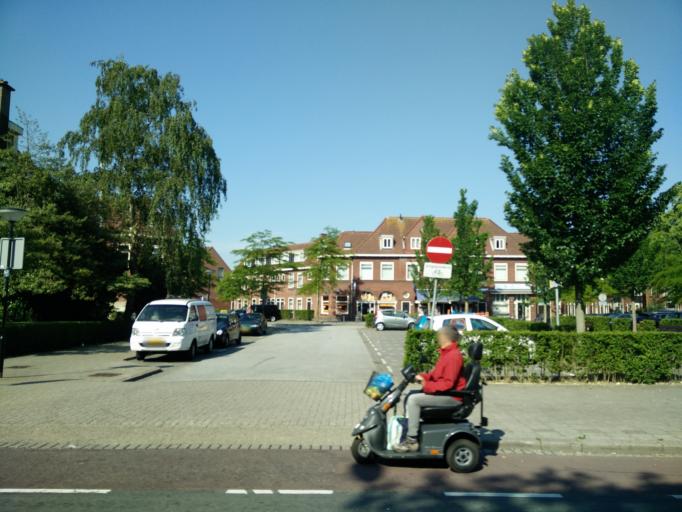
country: NL
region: South Holland
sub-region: Gemeente Dordrecht
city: Dordrecht
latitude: 51.8011
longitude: 4.6653
